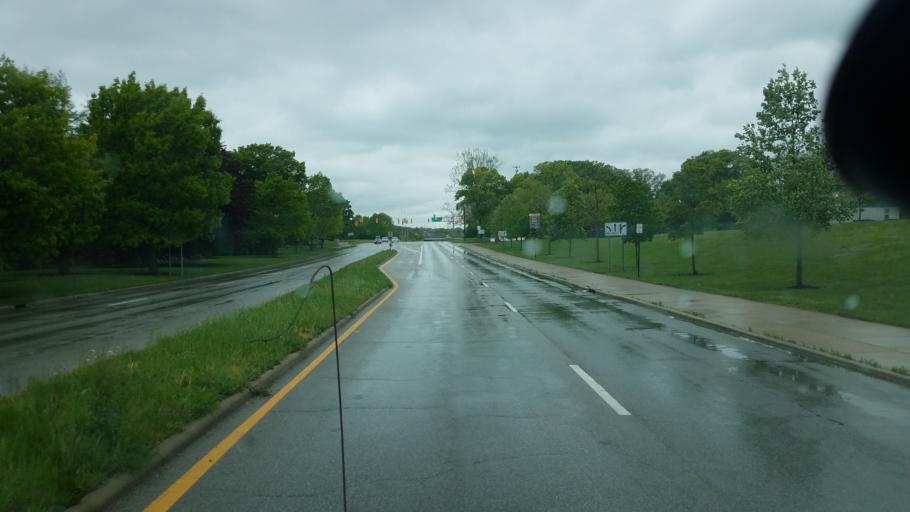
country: US
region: Ohio
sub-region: Franklin County
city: Grandview Heights
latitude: 40.0067
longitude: -83.0256
